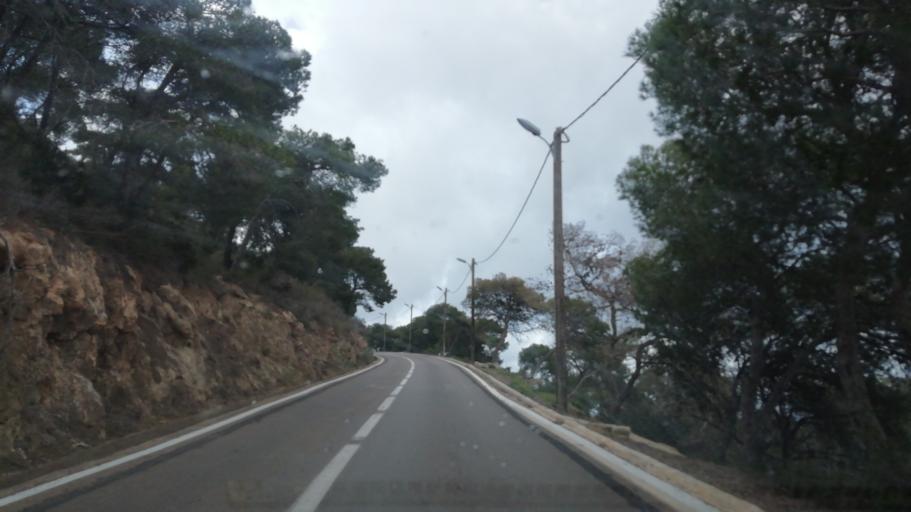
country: DZ
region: Oran
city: Oran
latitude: 35.7091
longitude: -0.6616
